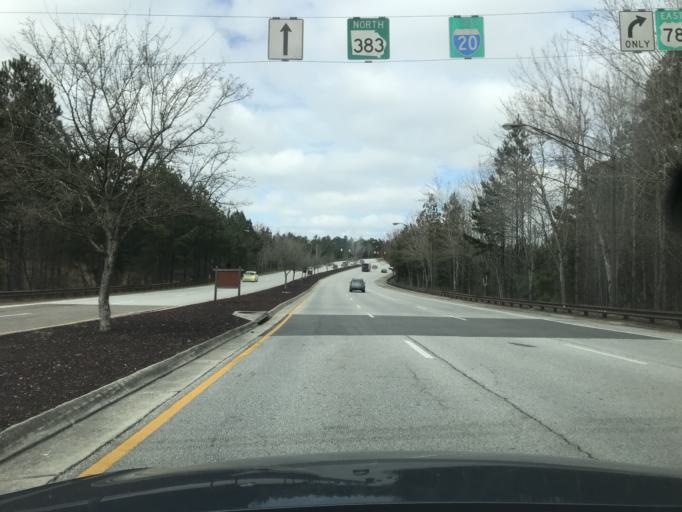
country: US
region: Georgia
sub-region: Columbia County
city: Grovetown
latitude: 33.4364
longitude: -82.1179
